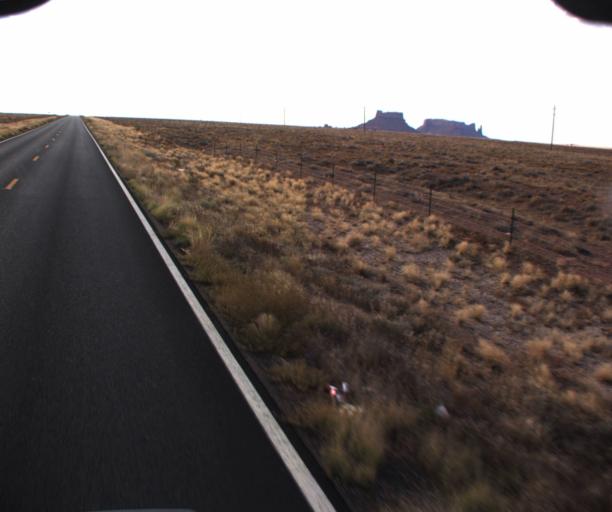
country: US
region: Arizona
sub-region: Apache County
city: Many Farms
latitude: 36.5734
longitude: -109.5495
